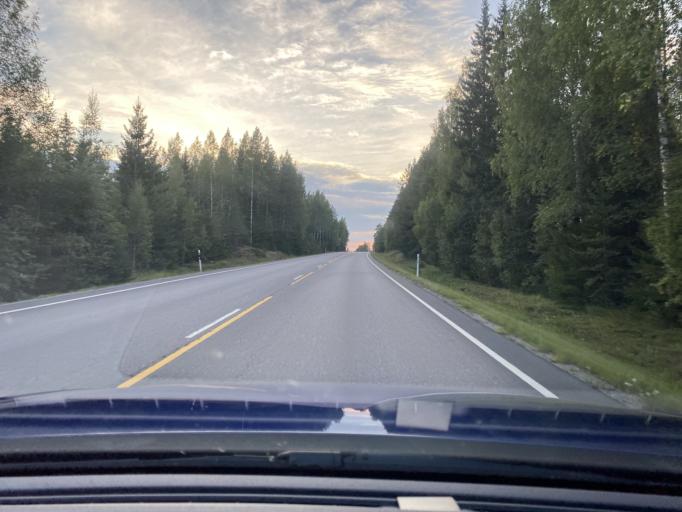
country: FI
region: Satakunta
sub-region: Pohjois-Satakunta
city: Kankaanpaeae
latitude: 61.7690
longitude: 22.4697
